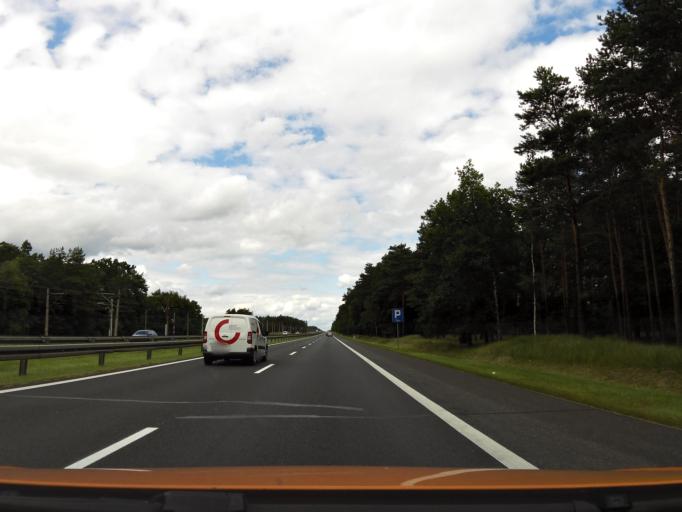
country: PL
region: West Pomeranian Voivodeship
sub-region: Powiat goleniowski
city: Goleniow
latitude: 53.4958
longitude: 14.7973
